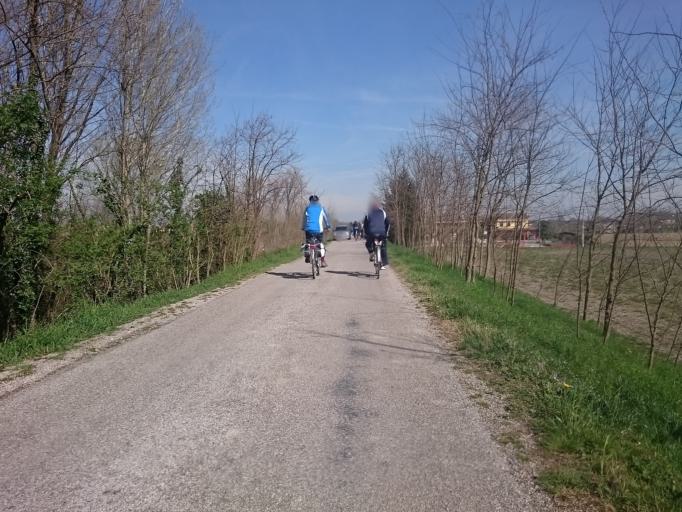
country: IT
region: Veneto
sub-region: Provincia di Padova
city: Sarmeola
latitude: 45.4234
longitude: 11.8286
